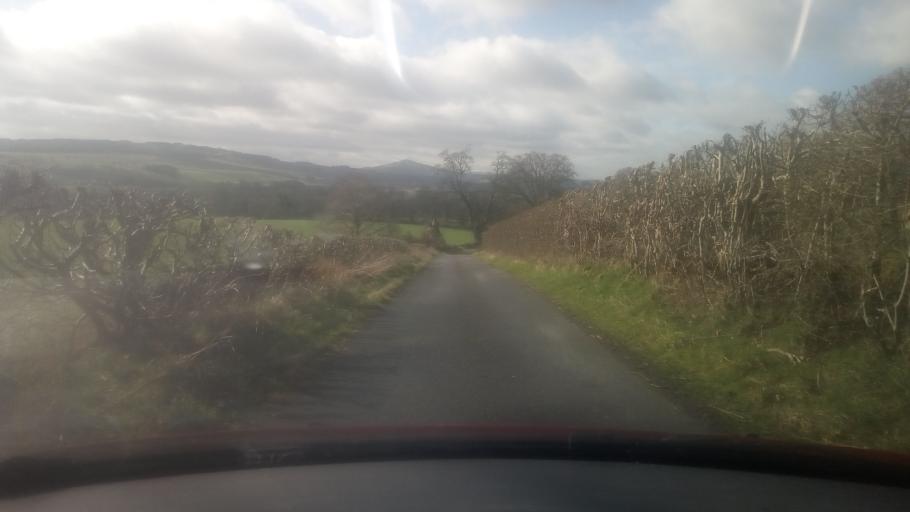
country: GB
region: Scotland
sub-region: The Scottish Borders
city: Jedburgh
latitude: 55.5215
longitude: -2.5774
